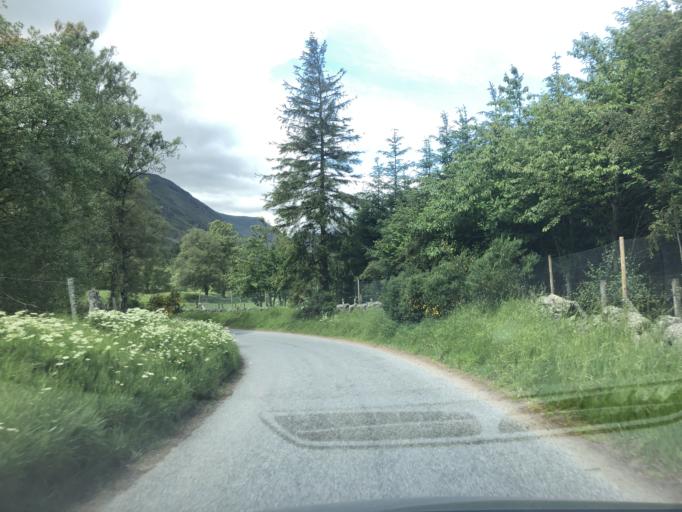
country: GB
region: Scotland
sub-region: Angus
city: Kirriemuir
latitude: 56.8384
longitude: -3.0994
